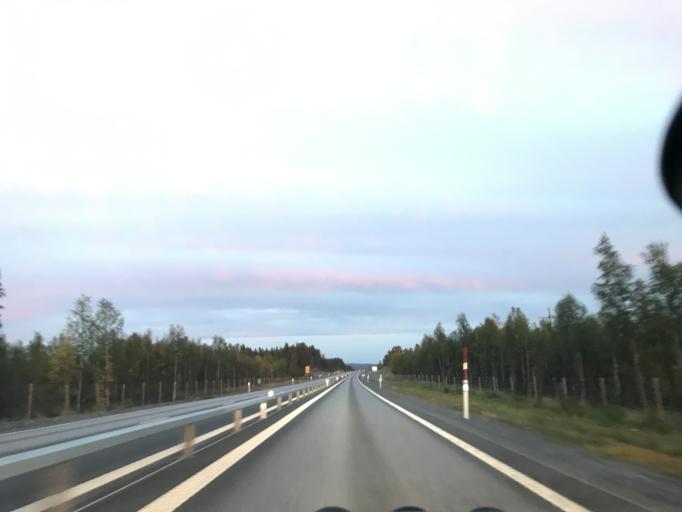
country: SE
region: Norrbotten
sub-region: Gallivare Kommun
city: Malmberget
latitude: 67.6857
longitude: 20.8560
